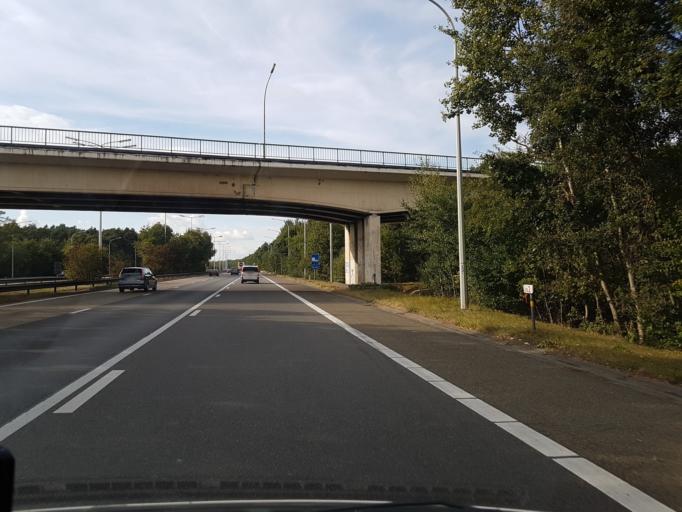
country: BE
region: Flanders
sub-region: Provincie Limburg
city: Genk
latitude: 50.9940
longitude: 5.4962
